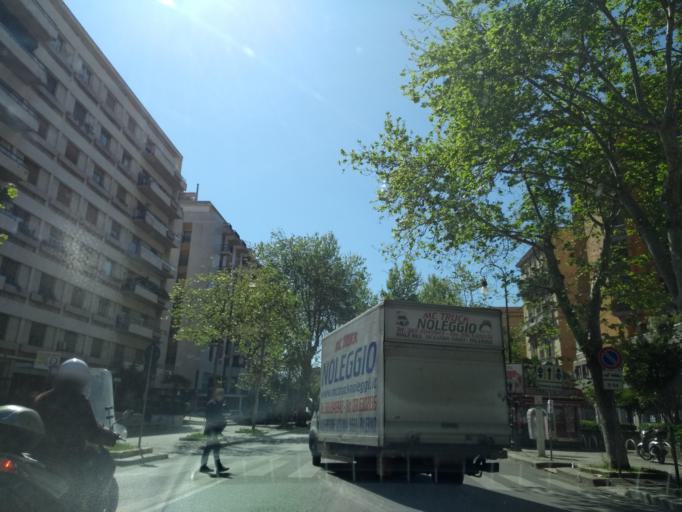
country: IT
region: Sicily
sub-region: Palermo
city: Palermo
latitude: 38.1355
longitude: 13.3486
